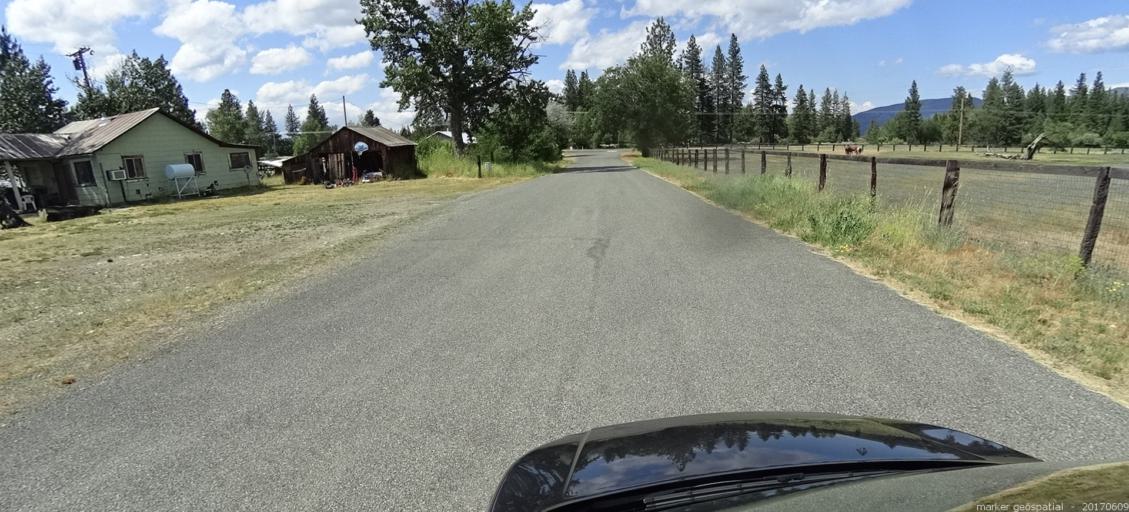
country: US
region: California
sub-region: Siskiyou County
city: Yreka
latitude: 41.4556
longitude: -122.8770
